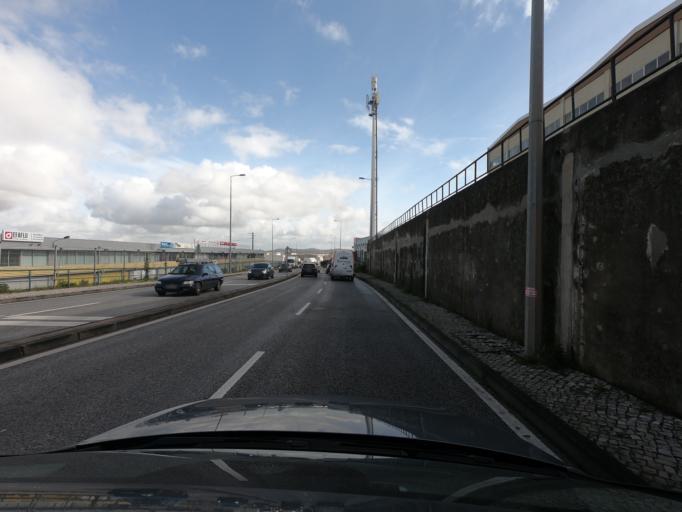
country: PT
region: Lisbon
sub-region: Sintra
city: Cacem
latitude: 38.7594
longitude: -9.3066
